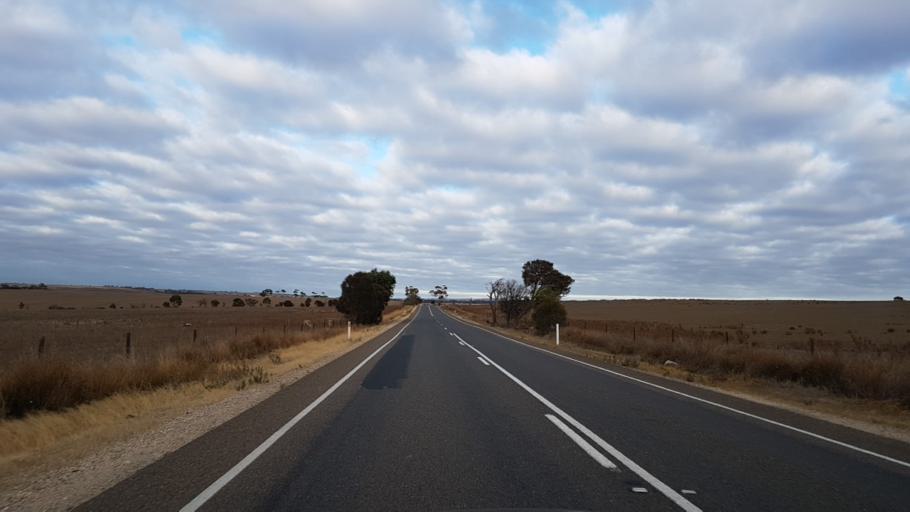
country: AU
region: South Australia
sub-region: Mount Barker
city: Callington
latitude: -35.1933
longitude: 138.9880
